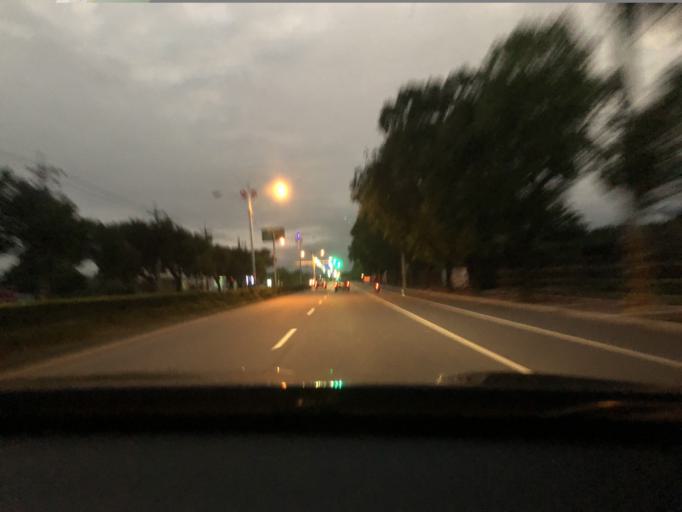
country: TW
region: Taiwan
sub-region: Hualien
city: Hualian
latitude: 23.9572
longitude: 121.5622
